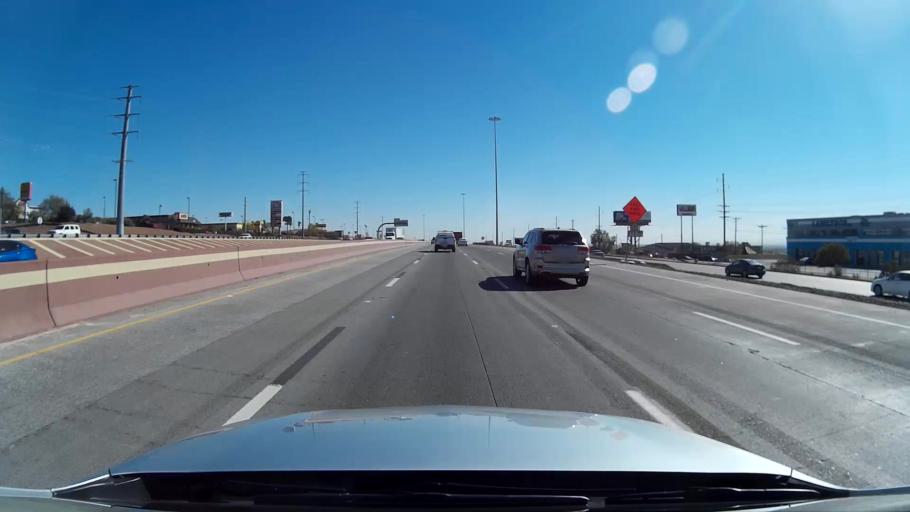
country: US
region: Texas
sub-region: El Paso County
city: Socorro
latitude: 31.7263
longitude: -106.3108
